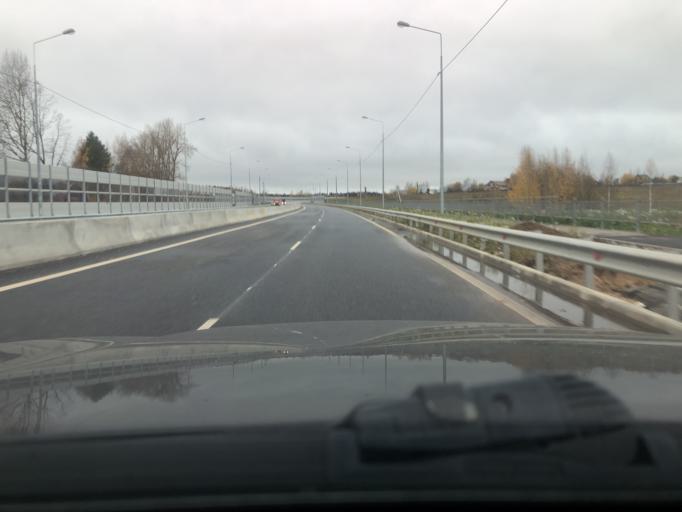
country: RU
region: Moskovskaya
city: Semkhoz
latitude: 56.3182
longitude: 38.0857
